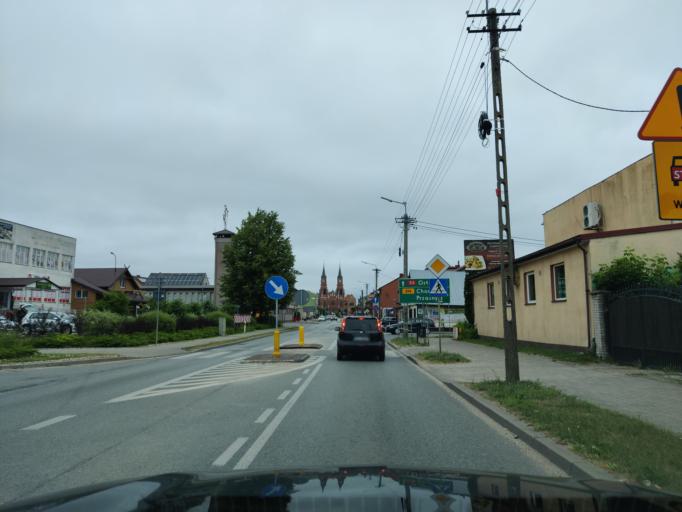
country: PL
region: Masovian Voivodeship
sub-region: Powiat ostrolecki
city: Myszyniec
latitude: 53.3848
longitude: 21.3400
